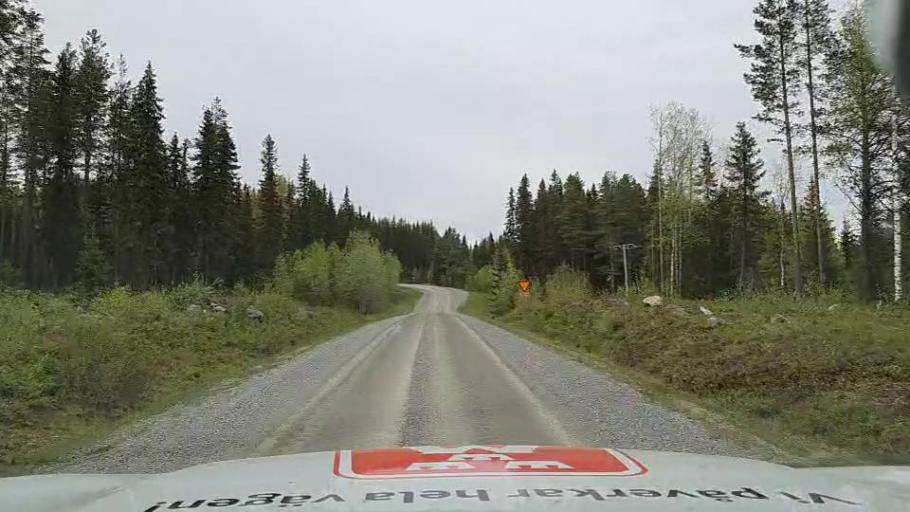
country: SE
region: Jaemtland
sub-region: OEstersunds Kommun
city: Brunflo
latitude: 62.6507
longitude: 14.9252
